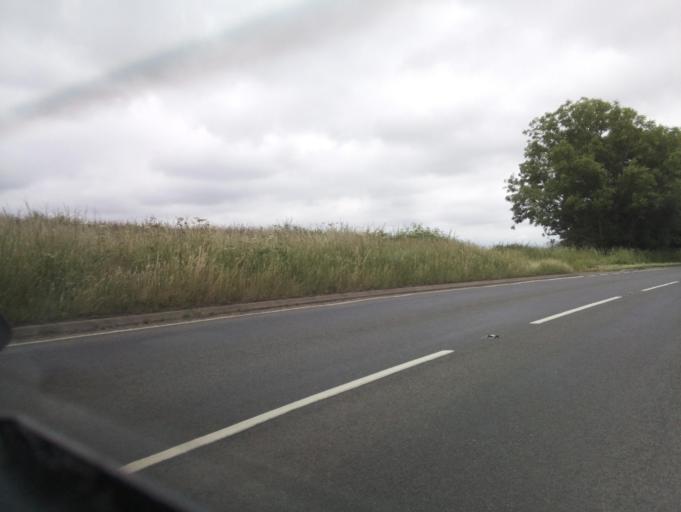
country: GB
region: England
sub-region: Leicestershire
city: Grimston
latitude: 52.7832
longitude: -1.0015
